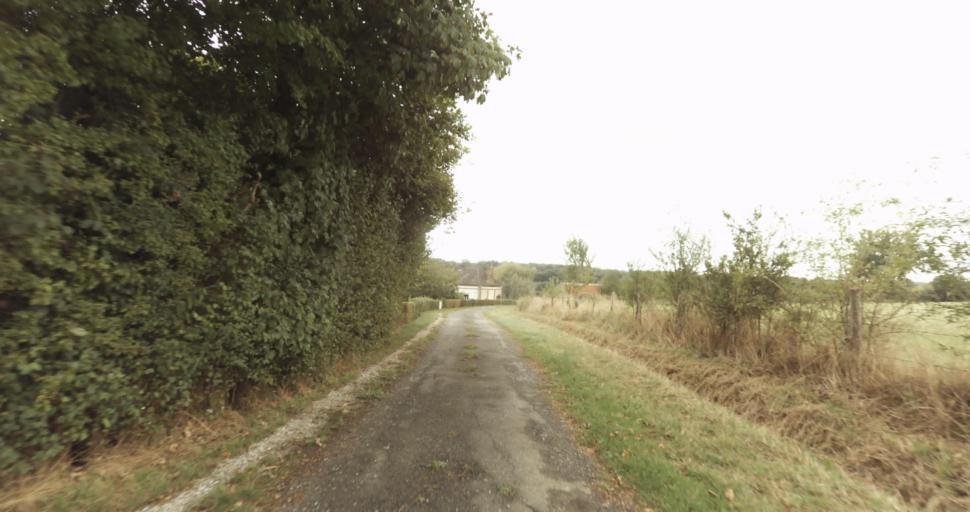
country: FR
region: Lower Normandy
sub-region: Departement de l'Orne
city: Sainte-Gauburge-Sainte-Colombe
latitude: 48.7193
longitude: 0.4522
